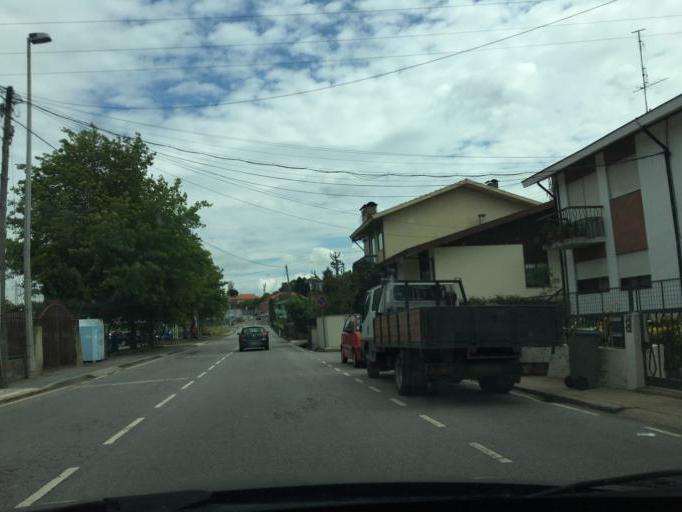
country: PT
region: Porto
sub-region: Maia
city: Maia
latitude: 41.2460
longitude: -8.6185
